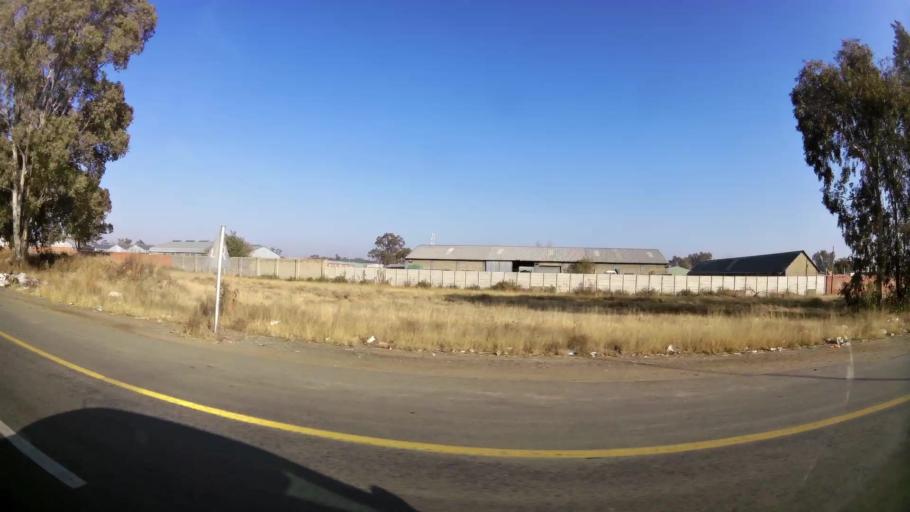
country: ZA
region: Orange Free State
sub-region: Mangaung Metropolitan Municipality
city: Bloemfontein
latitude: -29.1301
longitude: 26.2671
